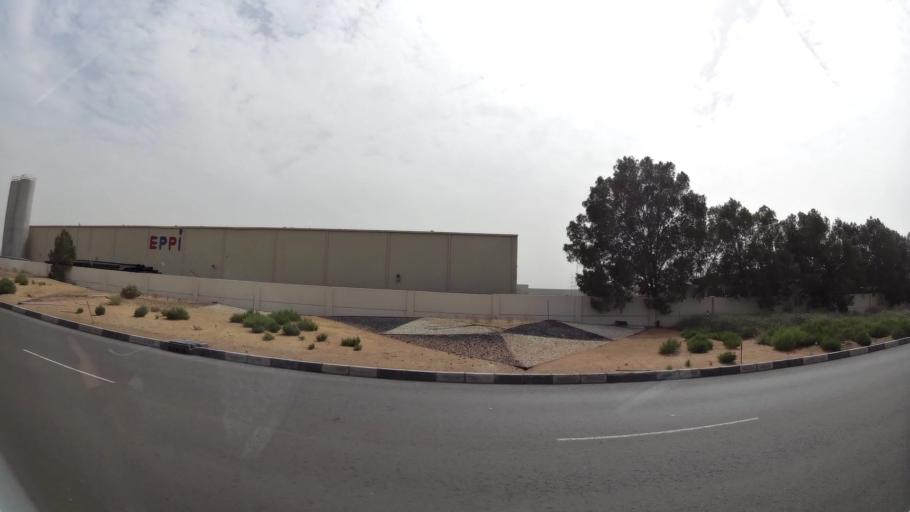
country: AE
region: Abu Dhabi
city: Abu Dhabi
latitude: 24.3237
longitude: 54.5132
